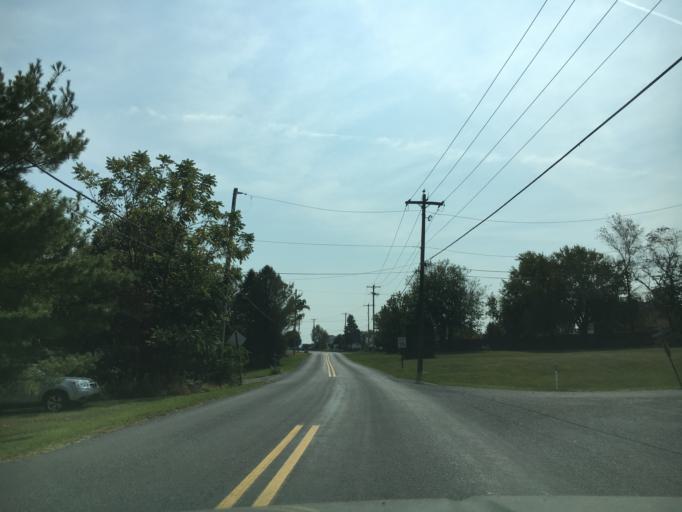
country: US
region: Pennsylvania
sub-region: Berks County
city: Topton
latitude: 40.5715
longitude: -75.7076
